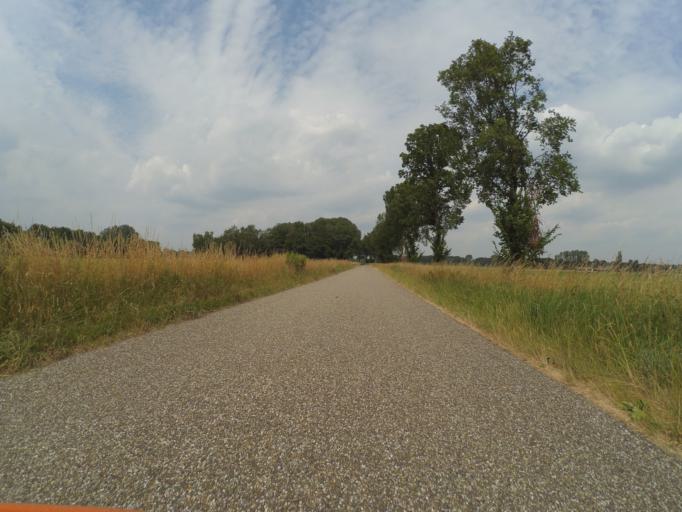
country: NL
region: Overijssel
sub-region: Gemeente Hof van Twente
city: Markelo
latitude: 52.1810
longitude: 6.4917
